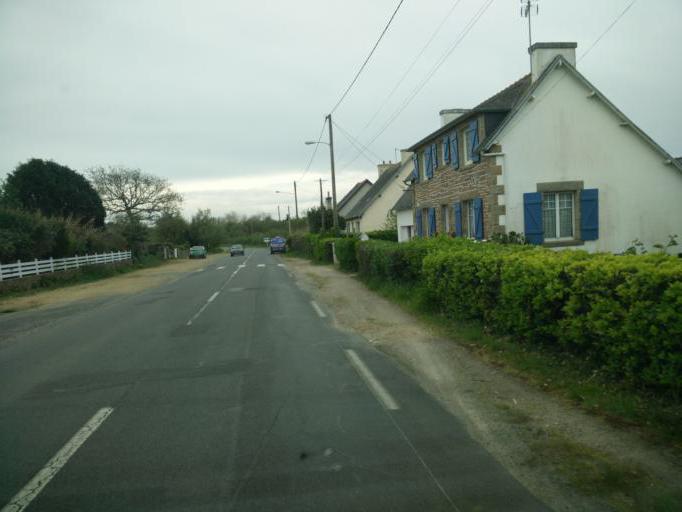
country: FR
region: Brittany
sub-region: Departement des Cotes-d'Armor
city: Tregastel
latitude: 48.8254
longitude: -3.5179
